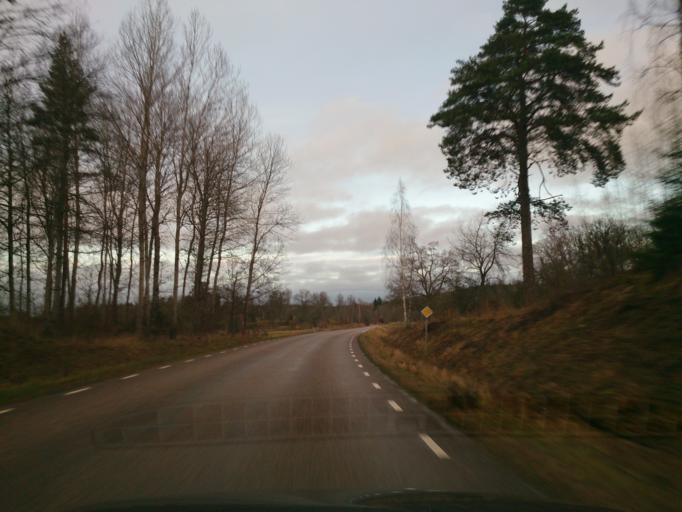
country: SE
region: OEstergoetland
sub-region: Atvidabergs Kommun
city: Atvidaberg
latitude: 58.3278
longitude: 16.0261
